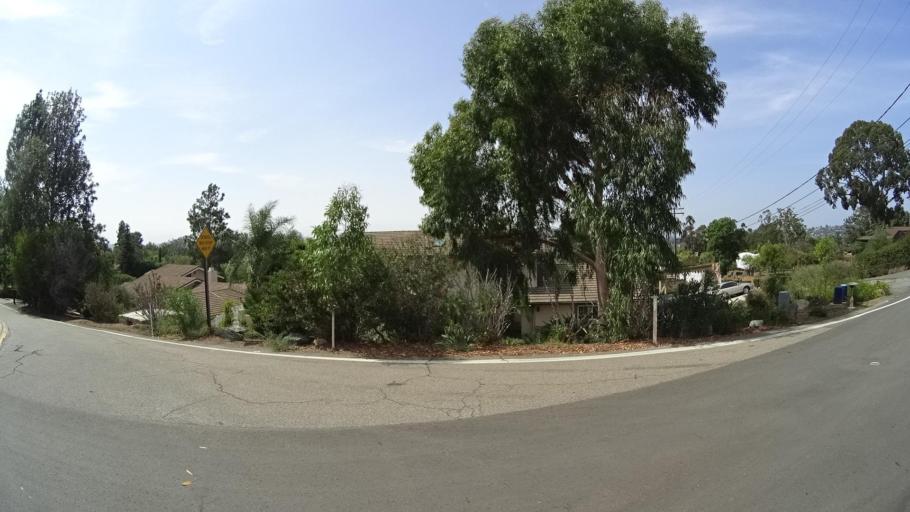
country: US
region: California
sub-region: San Diego County
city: Escondido
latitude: 33.0961
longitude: -117.0427
